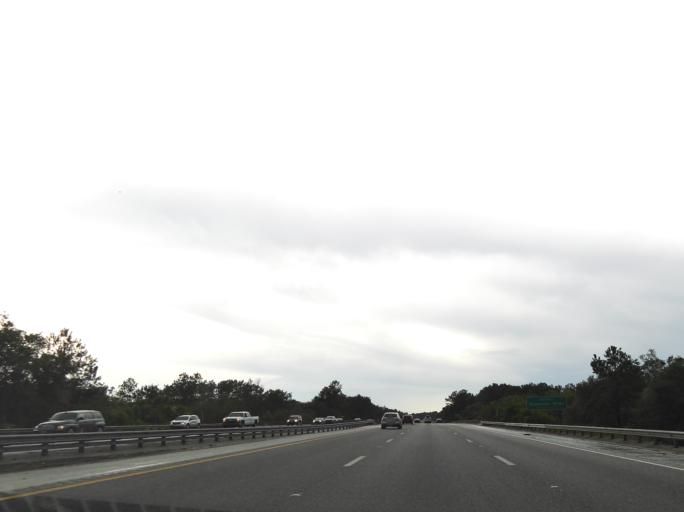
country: US
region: Florida
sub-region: Suwannee County
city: Wellborn
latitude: 30.3453
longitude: -82.8318
